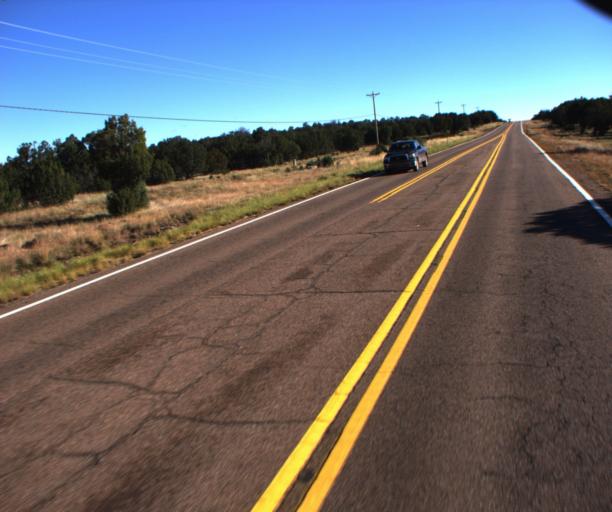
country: US
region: Arizona
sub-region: Navajo County
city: White Mountain Lake
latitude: 34.3034
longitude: -109.7845
